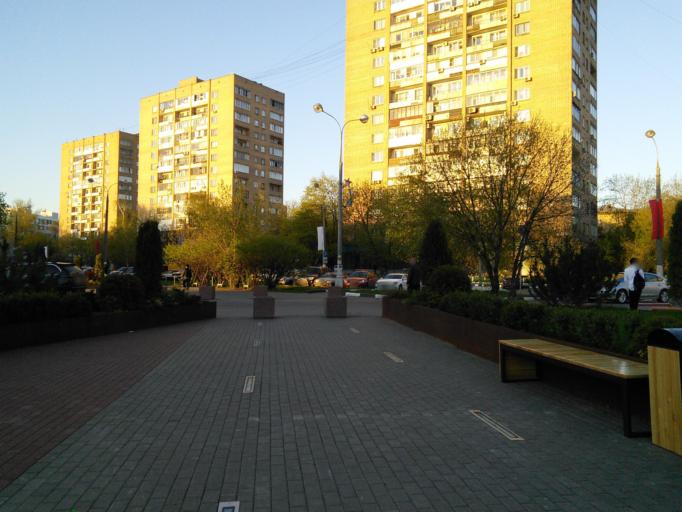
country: RU
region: Moskovskaya
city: Kozhukhovo
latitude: 55.7112
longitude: 37.6573
